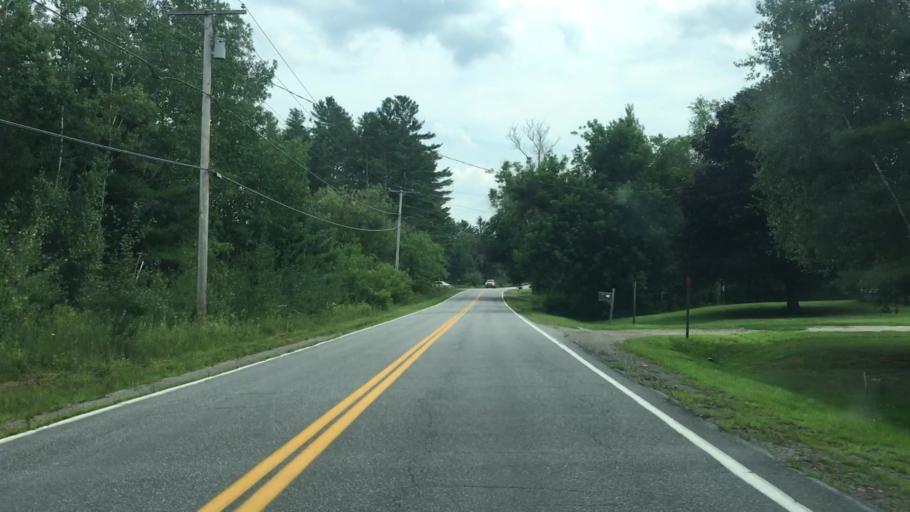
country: US
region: Maine
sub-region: Kennebec County
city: Vassalboro
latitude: 44.4671
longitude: -69.6147
